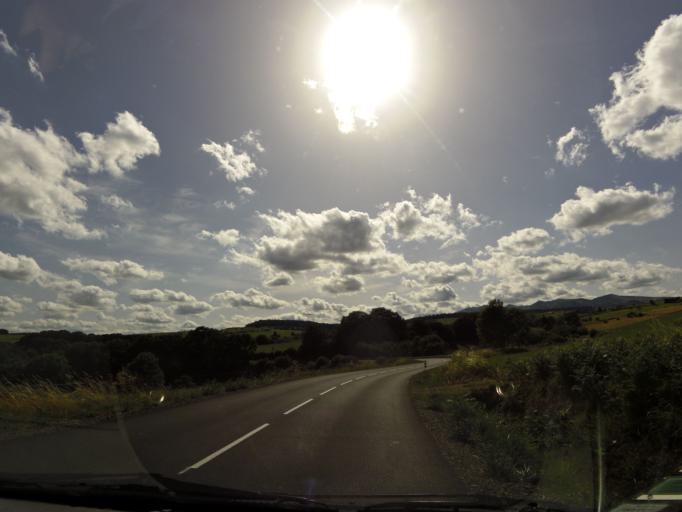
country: FR
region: Auvergne
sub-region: Departement du Puy-de-Dome
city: Aydat
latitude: 45.5463
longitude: 2.9450
